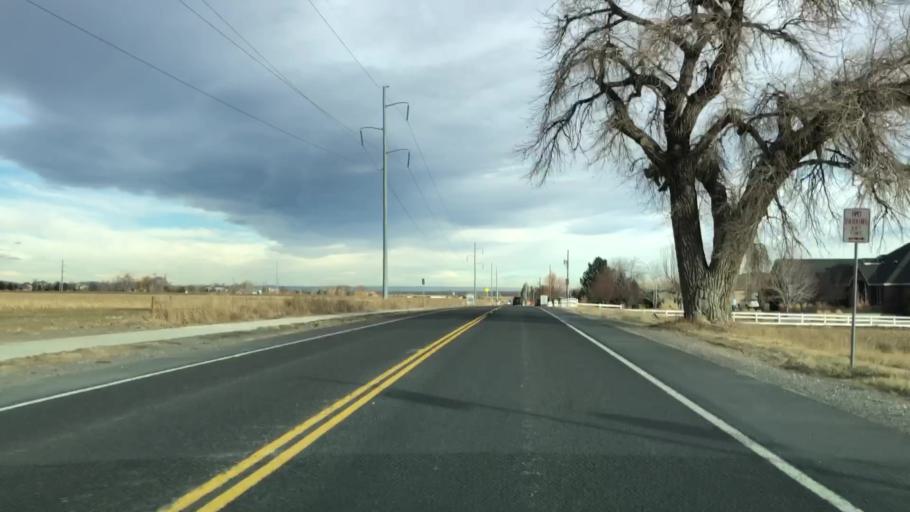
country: US
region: Colorado
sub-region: Larimer County
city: Loveland
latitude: 40.4588
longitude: -105.0441
